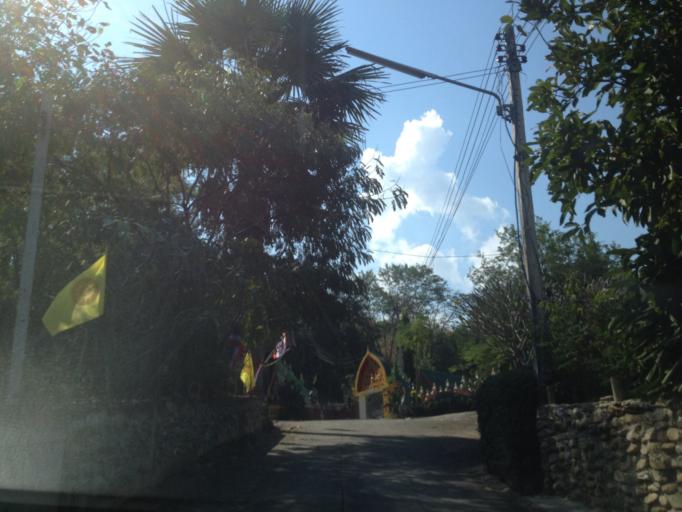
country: TH
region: Chiang Mai
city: Chom Thong
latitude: 18.3866
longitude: 98.6759
